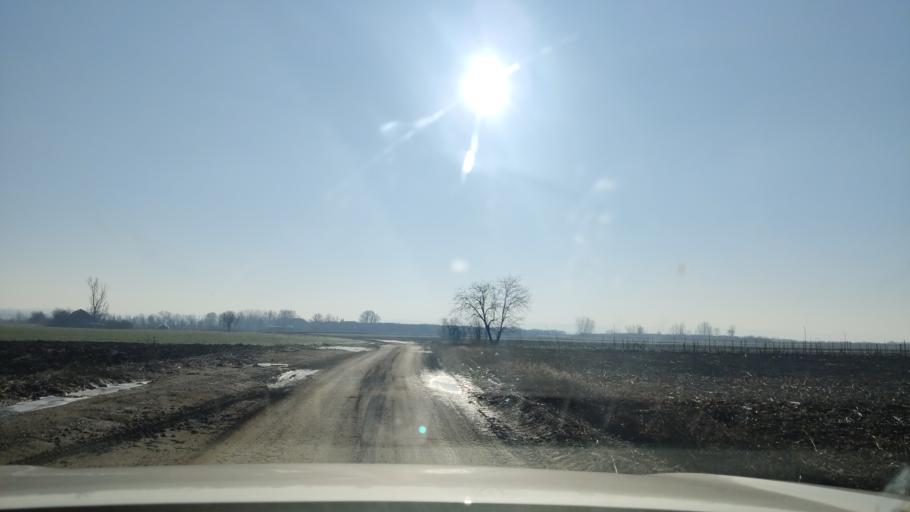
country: RS
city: Ostruznica
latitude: 44.7285
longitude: 20.2832
